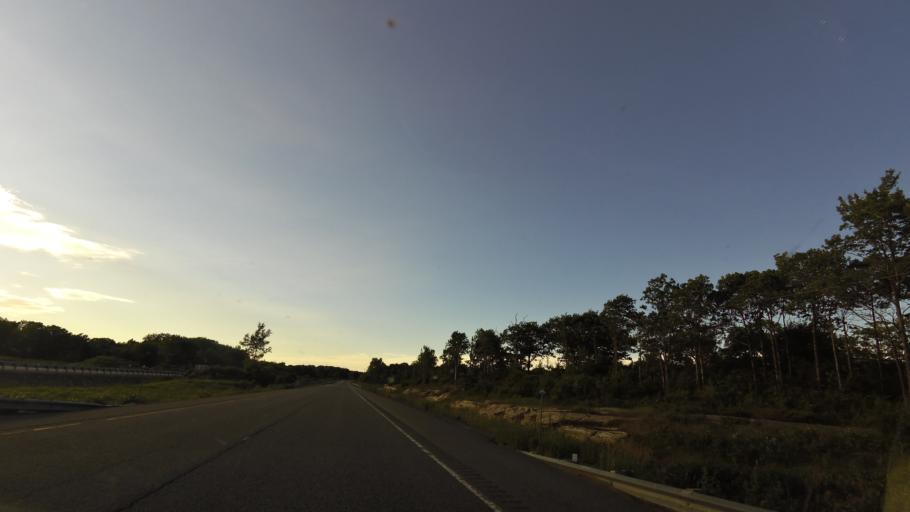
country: CA
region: Ontario
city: Midland
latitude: 44.8318
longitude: -79.7376
